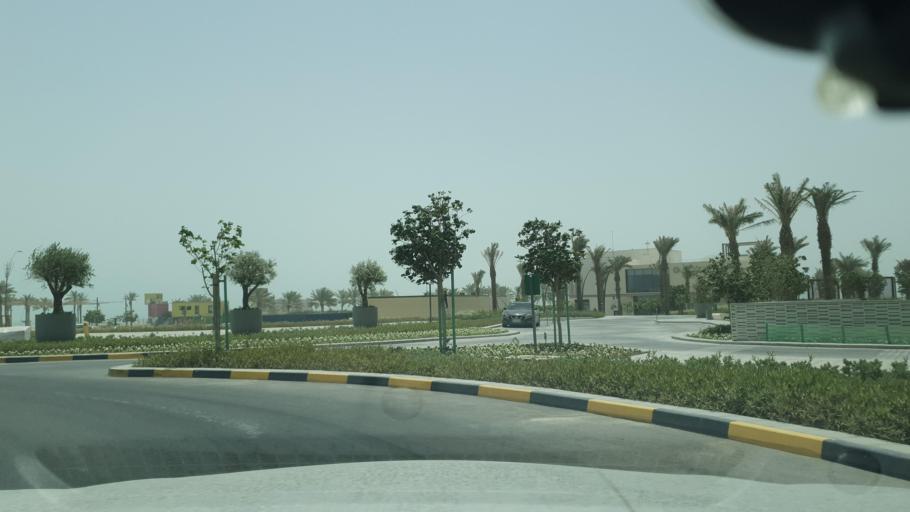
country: BH
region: Muharraq
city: Al Muharraq
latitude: 26.3044
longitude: 50.6449
